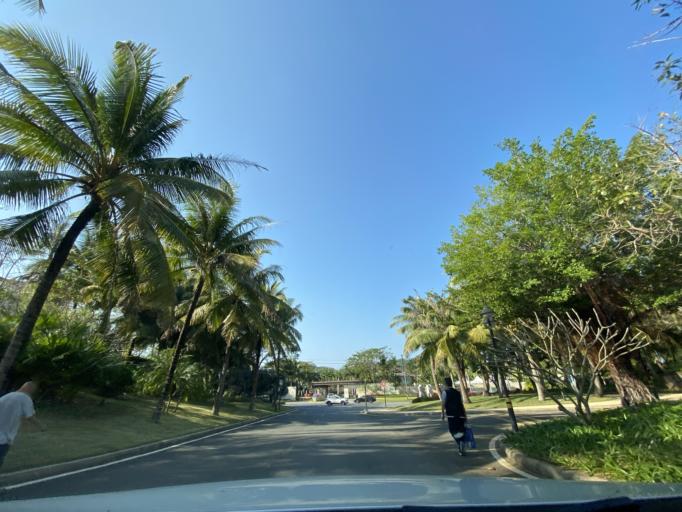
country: CN
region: Hainan
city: Yingzhou
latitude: 18.4185
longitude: 109.8962
